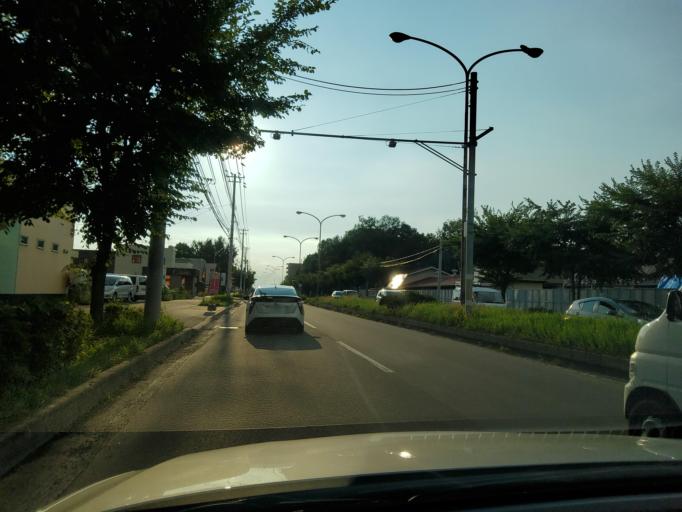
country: JP
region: Hokkaido
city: Obihiro
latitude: 42.9201
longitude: 143.1778
